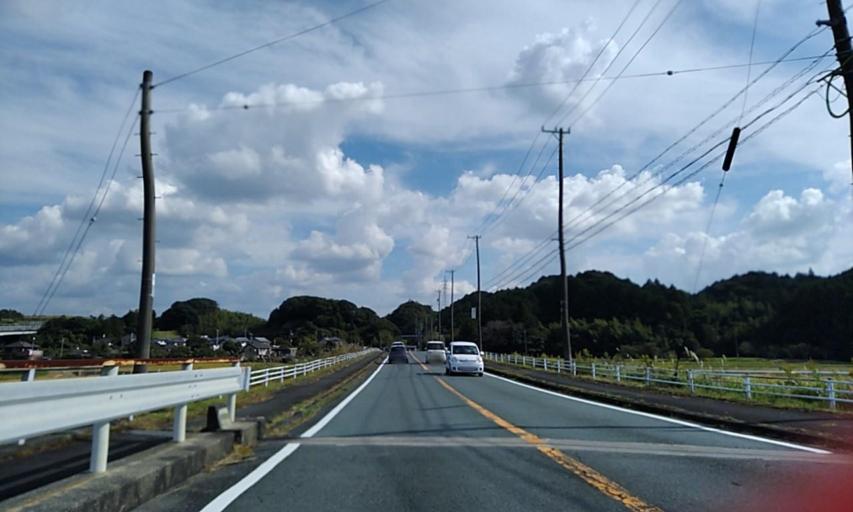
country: JP
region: Shizuoka
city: Mori
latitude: 34.8249
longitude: 137.8970
